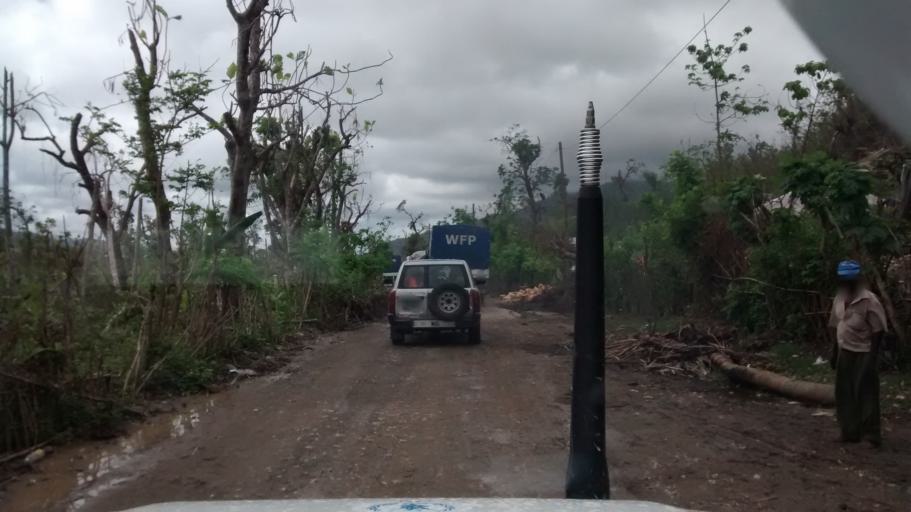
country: HT
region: Grandans
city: Jeremie
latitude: 18.5965
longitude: -74.1816
